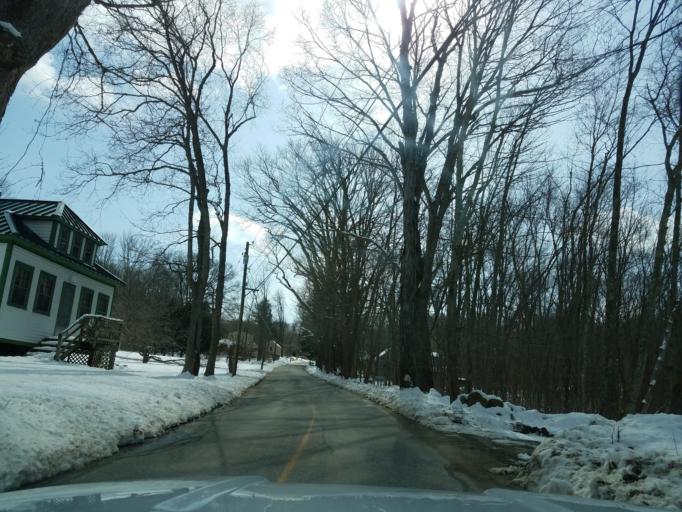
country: US
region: Connecticut
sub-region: Tolland County
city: Coventry Lake
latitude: 41.7272
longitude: -72.3581
